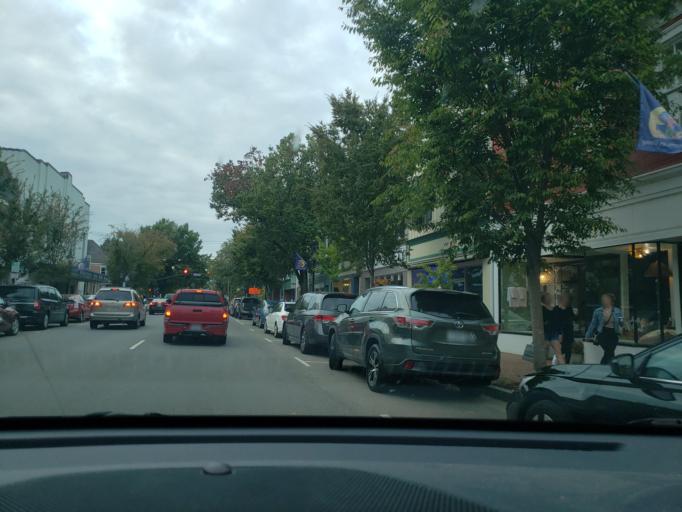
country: US
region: Virginia
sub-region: City of Fredericksburg
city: Fredericksburg
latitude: 38.3040
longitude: -77.4598
